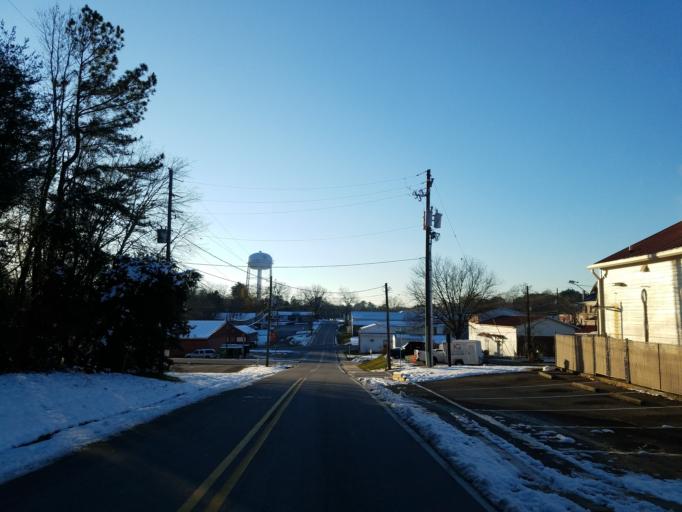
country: US
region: Georgia
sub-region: Dawson County
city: Dawsonville
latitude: 34.4205
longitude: -84.1173
